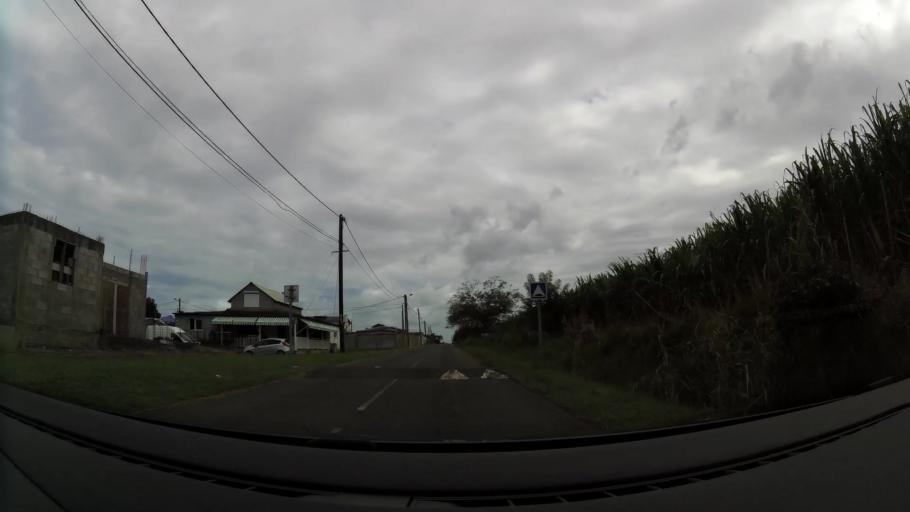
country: GP
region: Guadeloupe
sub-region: Guadeloupe
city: Sainte-Rose
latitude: 16.3244
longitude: -61.6996
